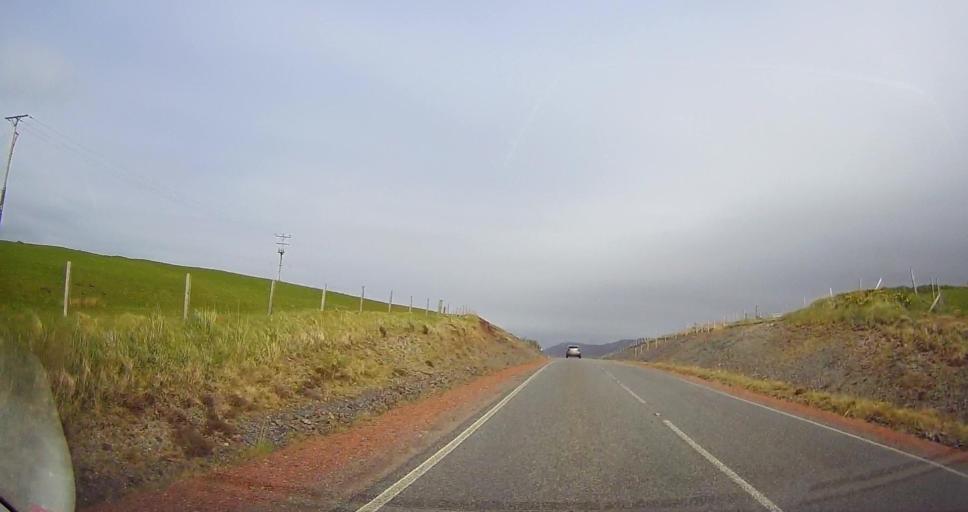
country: GB
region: Scotland
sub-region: Shetland Islands
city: Sandwick
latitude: 60.1202
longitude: -1.2891
